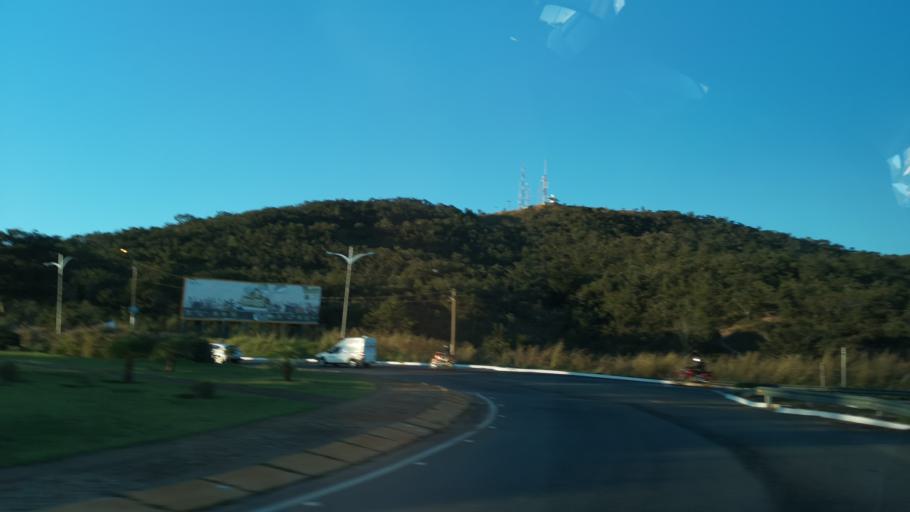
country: BR
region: Goias
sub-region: Senador Canedo
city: Senador Canedo
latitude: -16.6805
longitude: -49.1212
